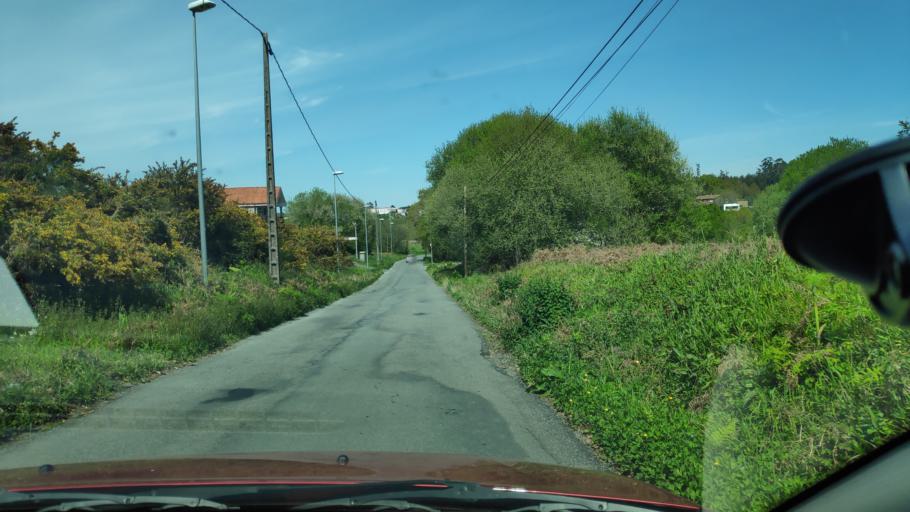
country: ES
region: Galicia
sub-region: Provincia da Coruna
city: Santiago de Compostela
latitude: 42.8925
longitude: -8.5257
